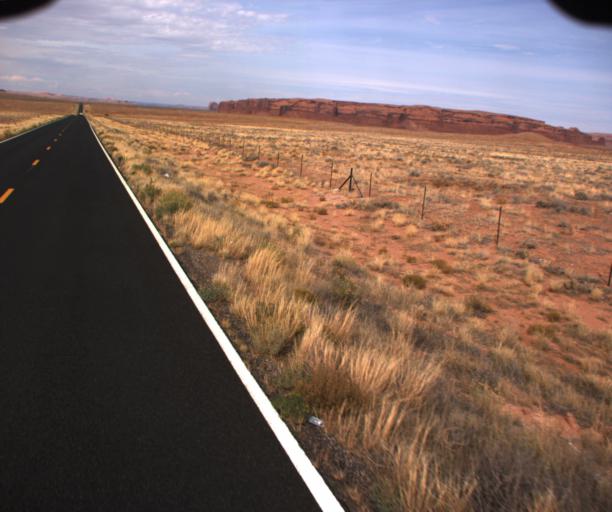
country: US
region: Arizona
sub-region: Apache County
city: Many Farms
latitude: 36.5722
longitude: -109.5486
